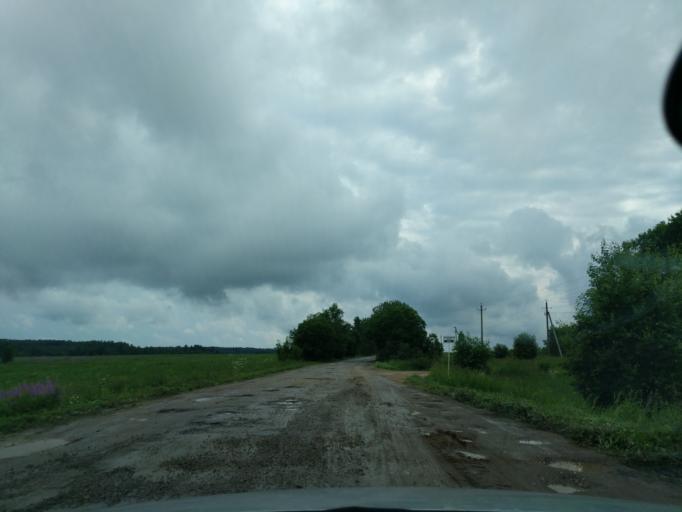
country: RU
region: Kaluga
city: Myatlevo
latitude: 54.7877
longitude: 35.7341
